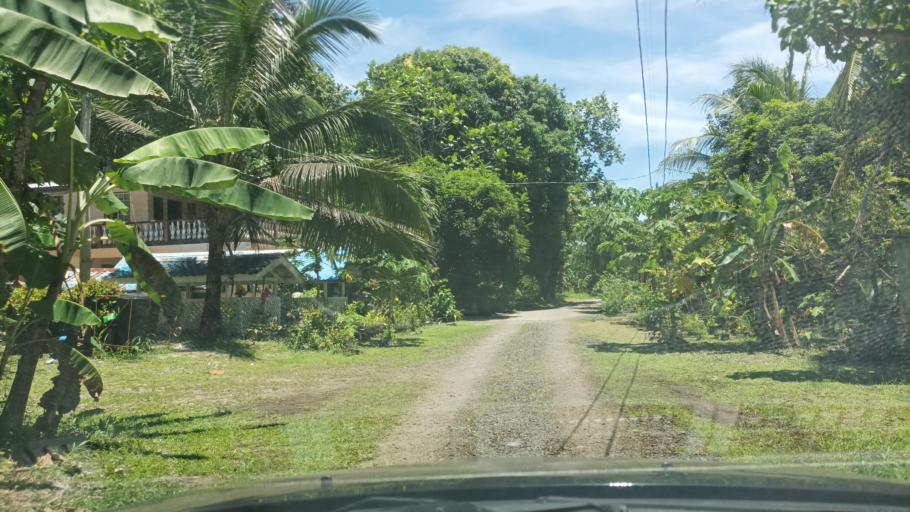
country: FM
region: Kosrae
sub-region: Lelu Municipality
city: Lelu
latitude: 5.3299
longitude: 163.0319
